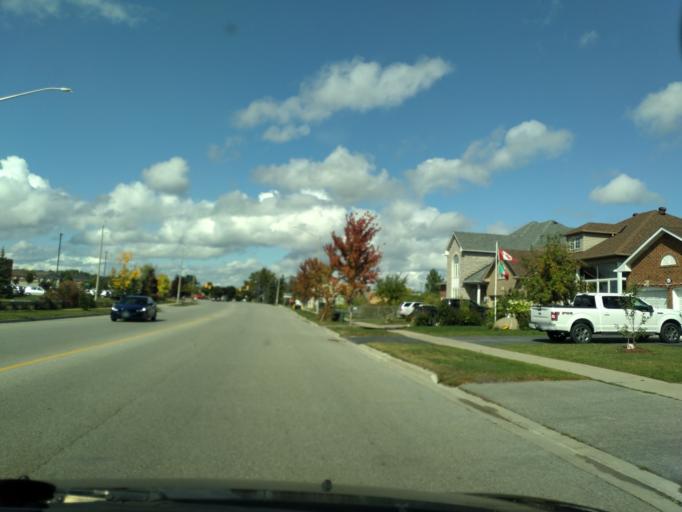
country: CA
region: Ontario
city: Innisfil
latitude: 44.3106
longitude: -79.5581
